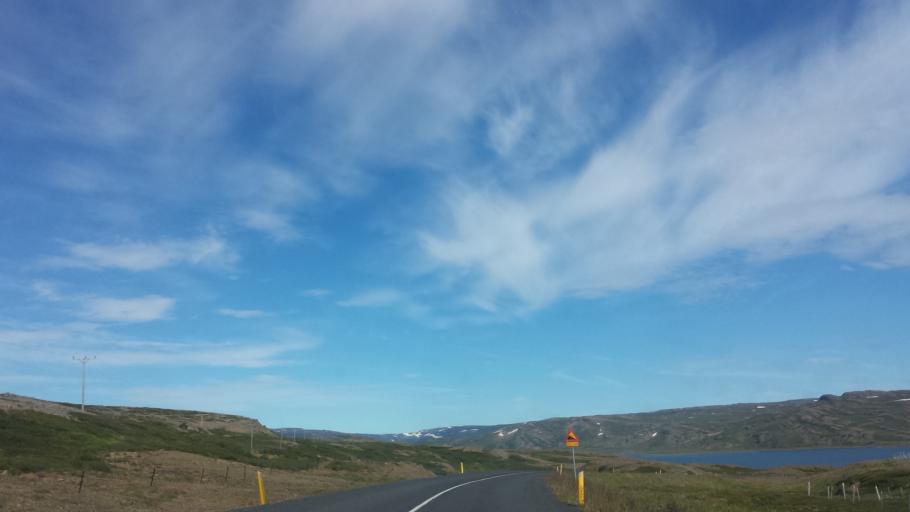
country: IS
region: West
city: Stykkisholmur
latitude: 65.7415
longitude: -21.7085
